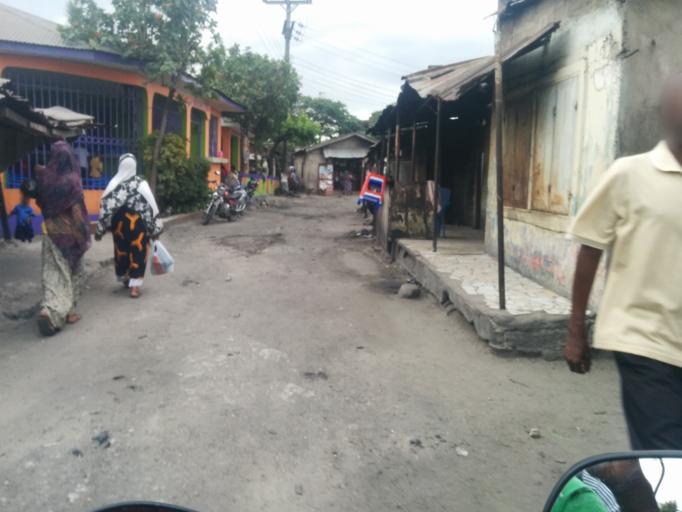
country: TZ
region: Dar es Salaam
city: Dar es Salaam
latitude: -6.8360
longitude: 39.2760
